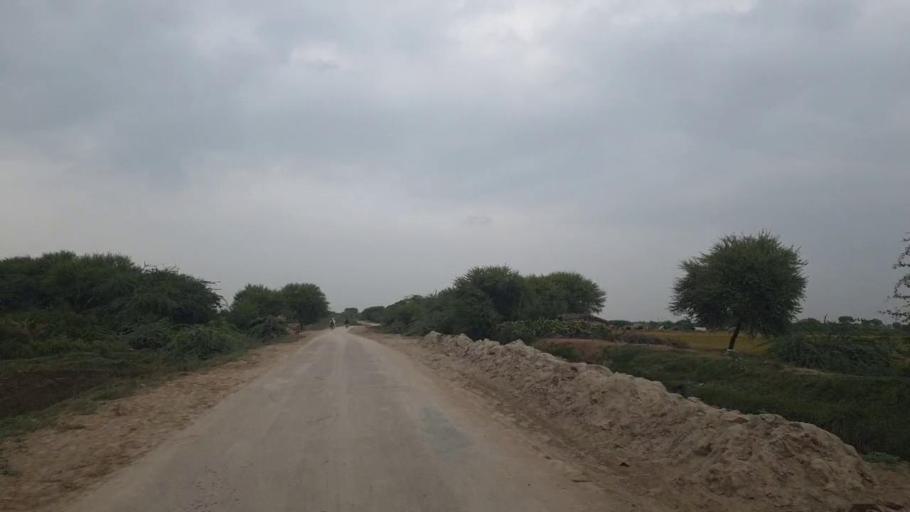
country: PK
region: Sindh
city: Badin
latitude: 24.6454
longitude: 68.6807
